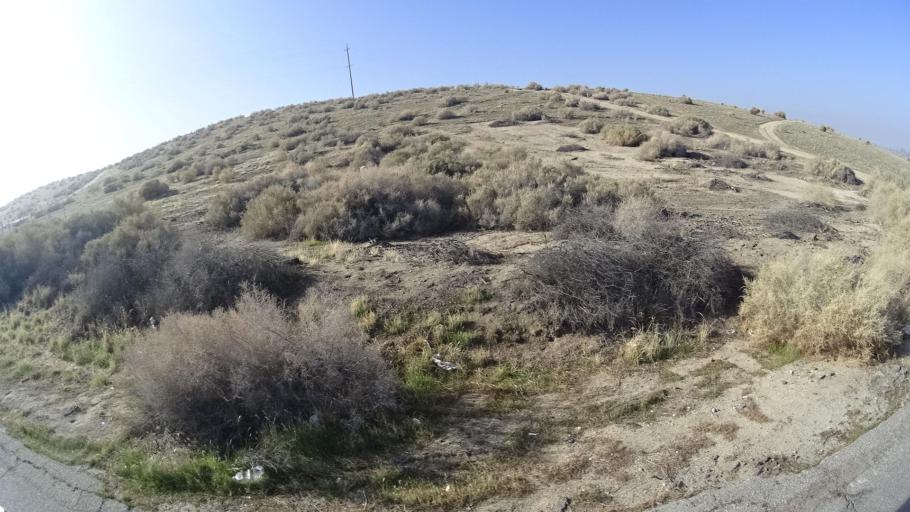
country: US
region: California
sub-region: Kern County
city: South Taft
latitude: 35.1234
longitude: -119.4549
